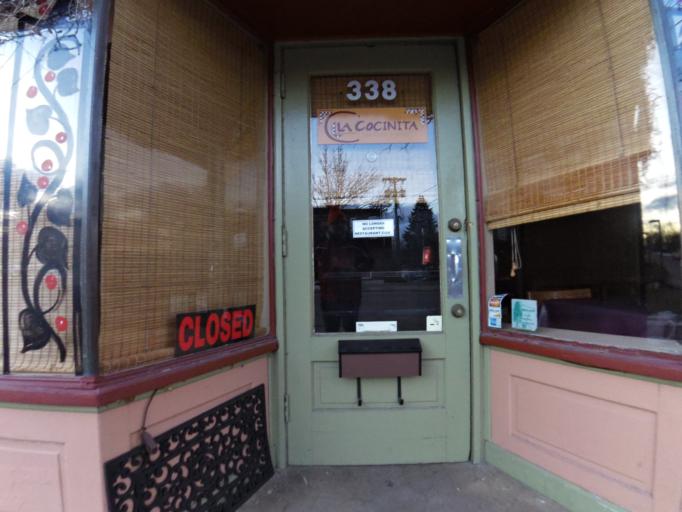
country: US
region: Minnesota
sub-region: Washington County
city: Bayport
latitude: 45.0216
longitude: -92.7818
